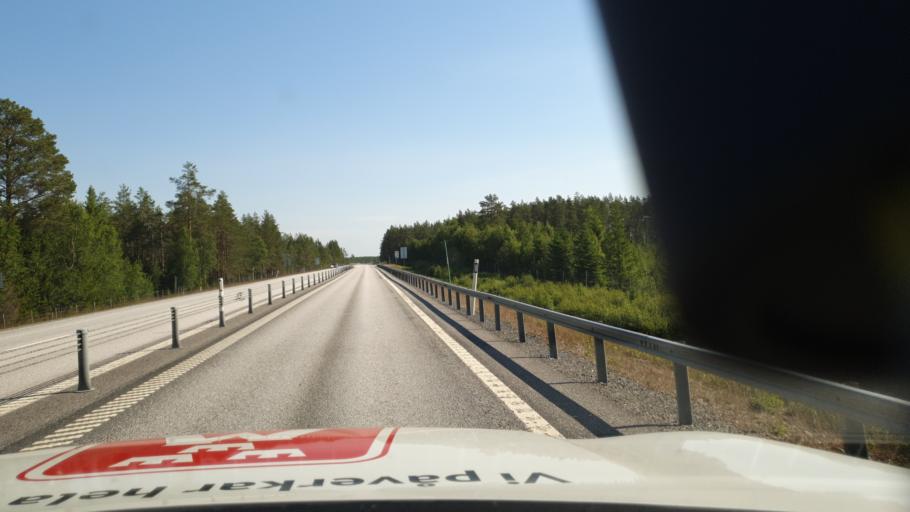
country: SE
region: Vaesterbotten
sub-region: Umea Kommun
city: Saevar
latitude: 63.9721
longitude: 20.7139
